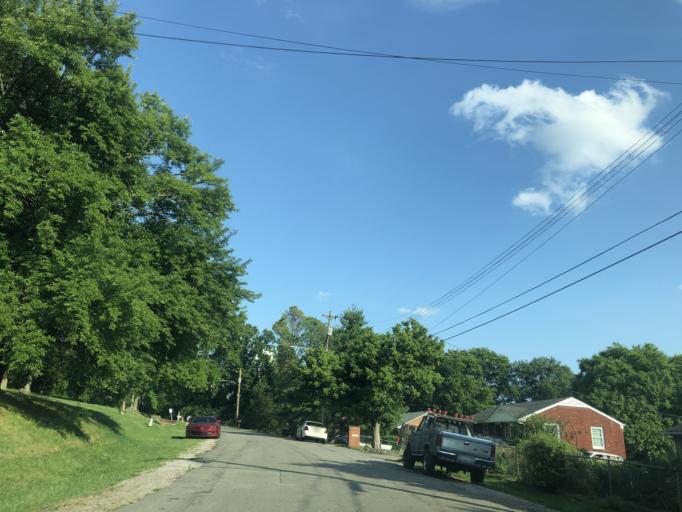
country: US
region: Tennessee
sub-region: Davidson County
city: Nashville
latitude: 36.2296
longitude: -86.7871
